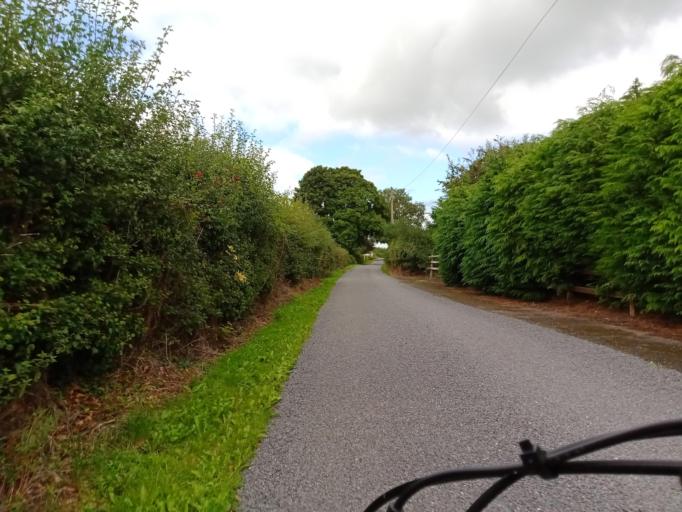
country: IE
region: Leinster
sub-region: Kilkenny
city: Callan
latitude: 52.5309
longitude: -7.2875
